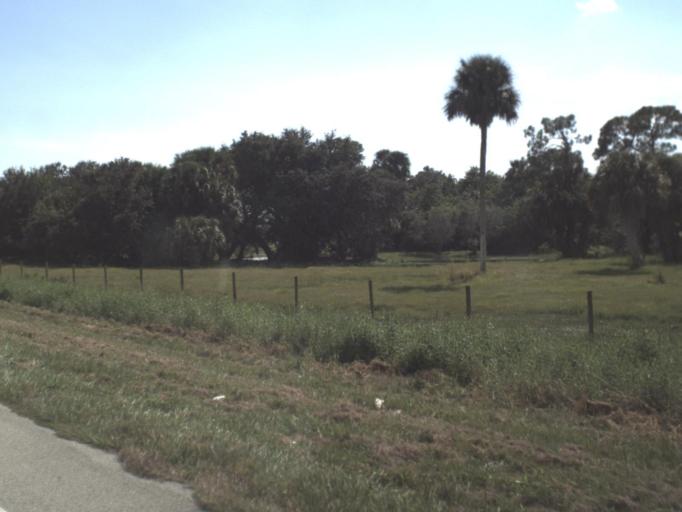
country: US
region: Florida
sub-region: Okeechobee County
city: Okeechobee
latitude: 27.2774
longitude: -80.8749
